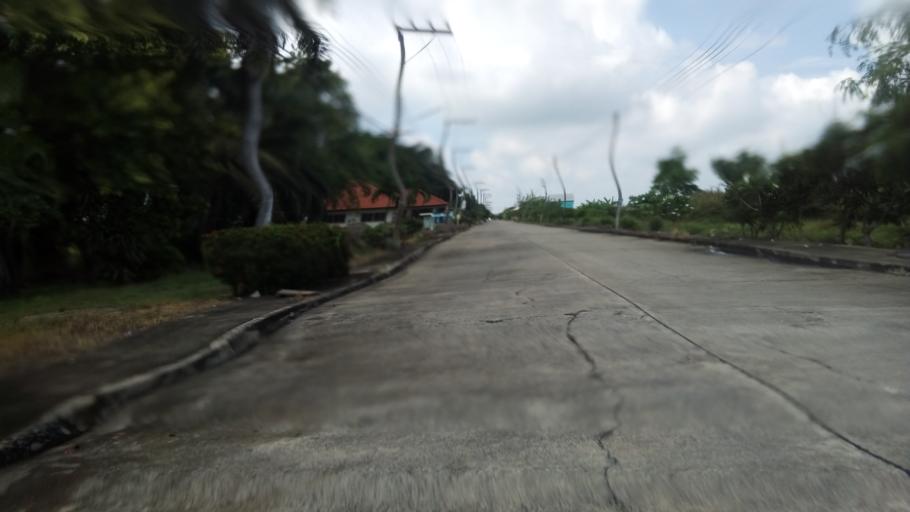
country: TH
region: Pathum Thani
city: Nong Suea
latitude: 14.0570
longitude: 100.8602
